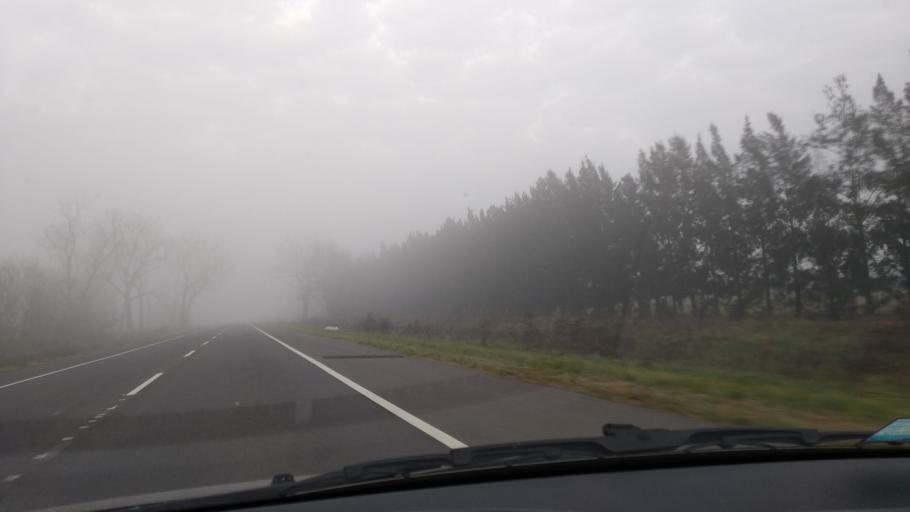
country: AR
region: Buenos Aires
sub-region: Partido de Brandsen
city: Brandsen
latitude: -35.1999
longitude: -58.3940
